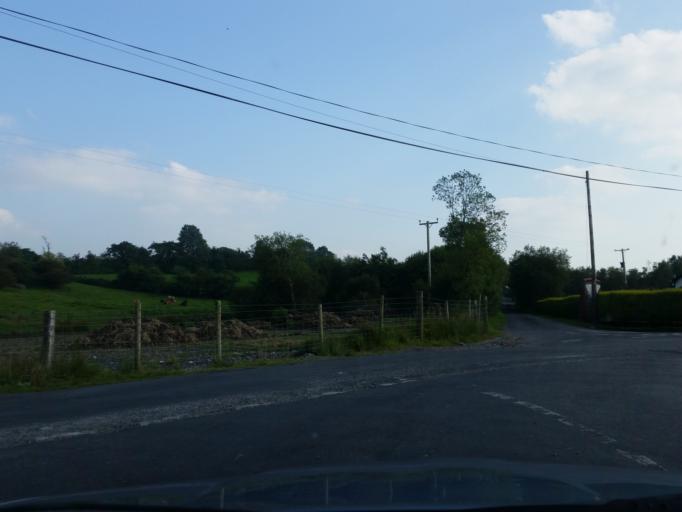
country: GB
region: Northern Ireland
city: Ballinamallard
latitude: 54.3365
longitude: -7.5362
